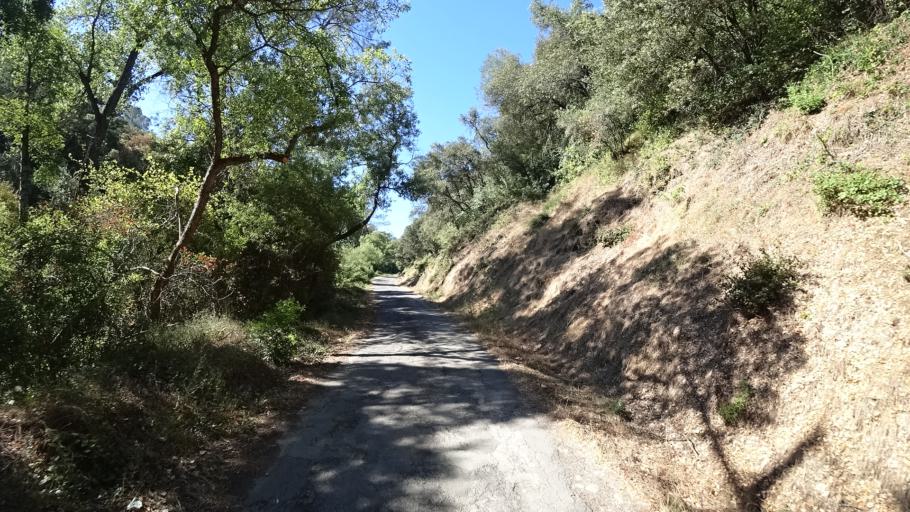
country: US
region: California
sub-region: Amador County
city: Jackson
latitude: 38.2767
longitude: -120.7584
